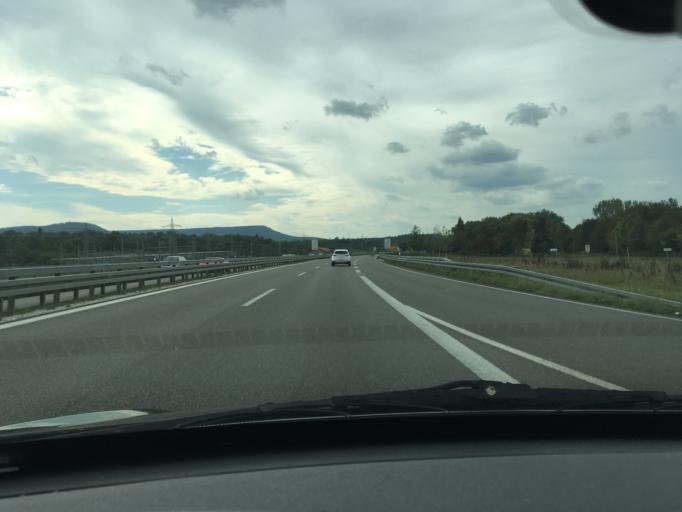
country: DE
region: Baden-Wuerttemberg
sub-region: Tuebingen Region
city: Dusslingen
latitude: 48.4395
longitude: 9.0573
